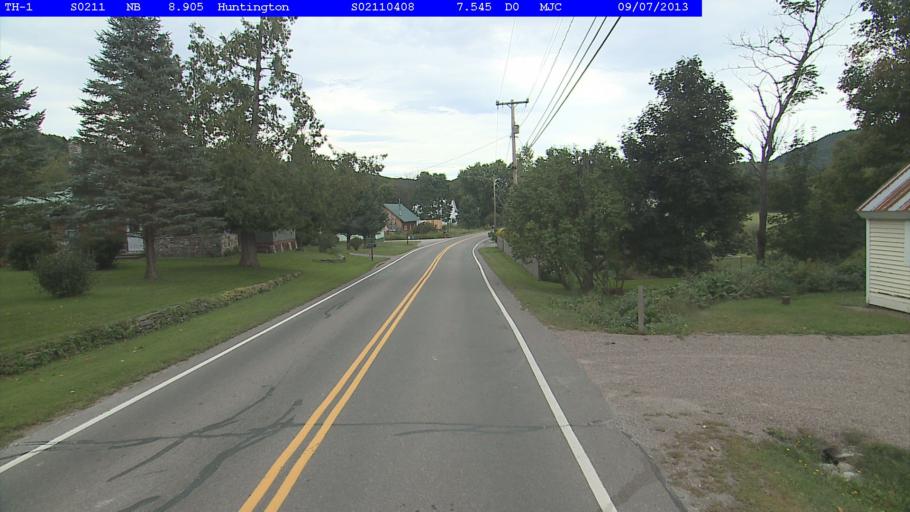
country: US
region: Vermont
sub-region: Chittenden County
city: Hinesburg
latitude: 44.3268
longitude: -72.9877
